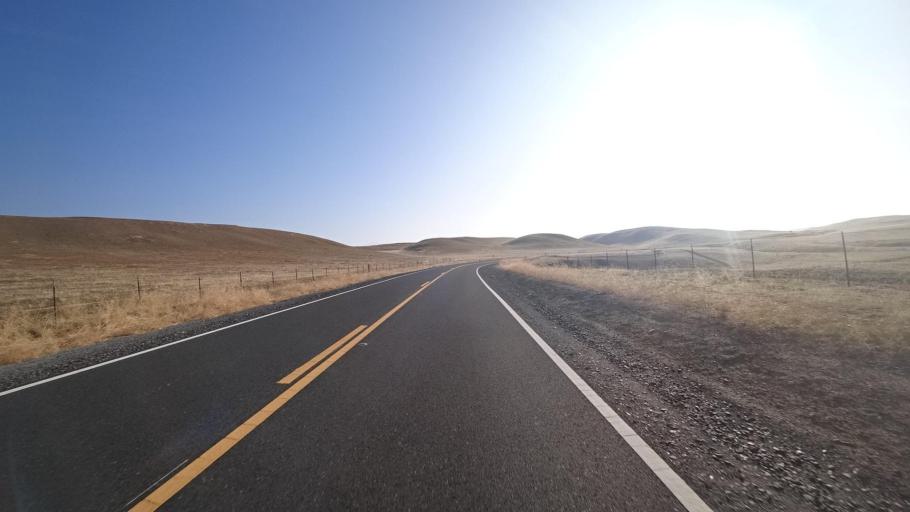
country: US
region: California
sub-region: Tulare County
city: Richgrove
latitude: 35.7457
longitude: -118.9656
